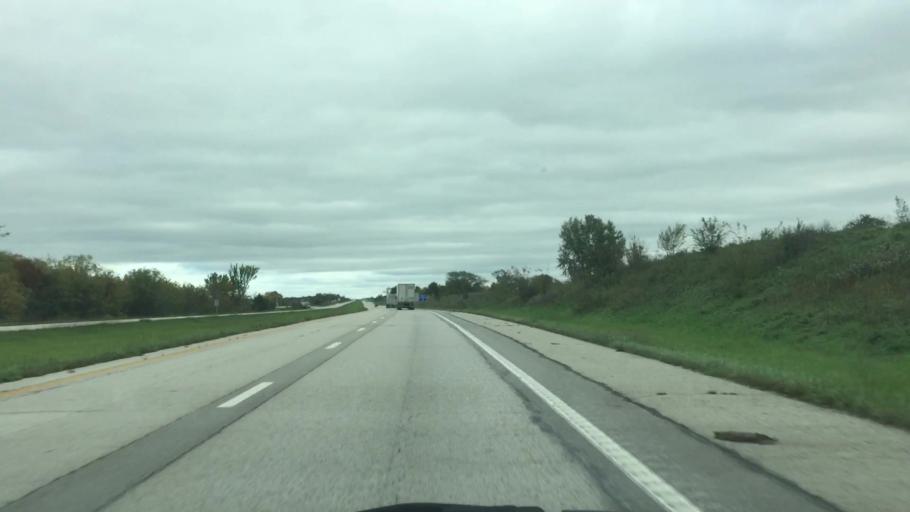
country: US
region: Missouri
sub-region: Harrison County
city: Bethany
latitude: 40.1103
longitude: -94.0660
